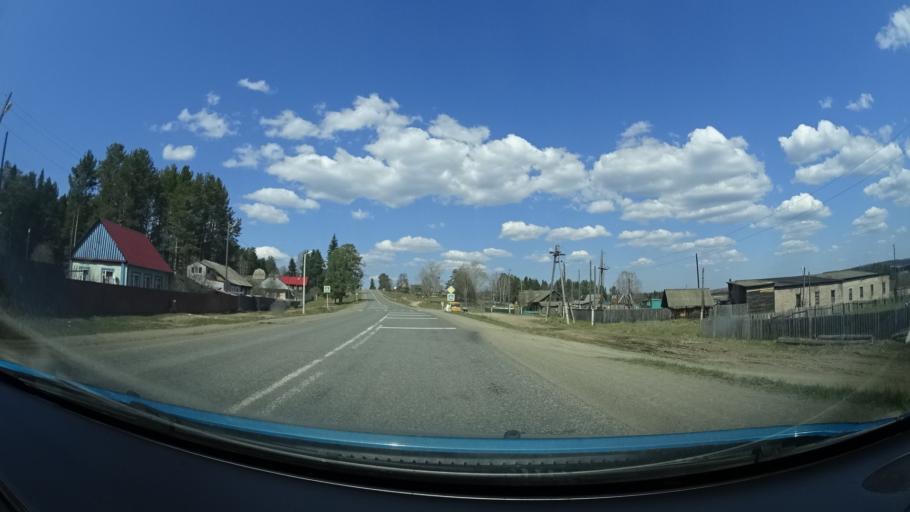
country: RU
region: Perm
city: Yugo-Kamskiy
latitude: 57.5527
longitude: 55.6856
